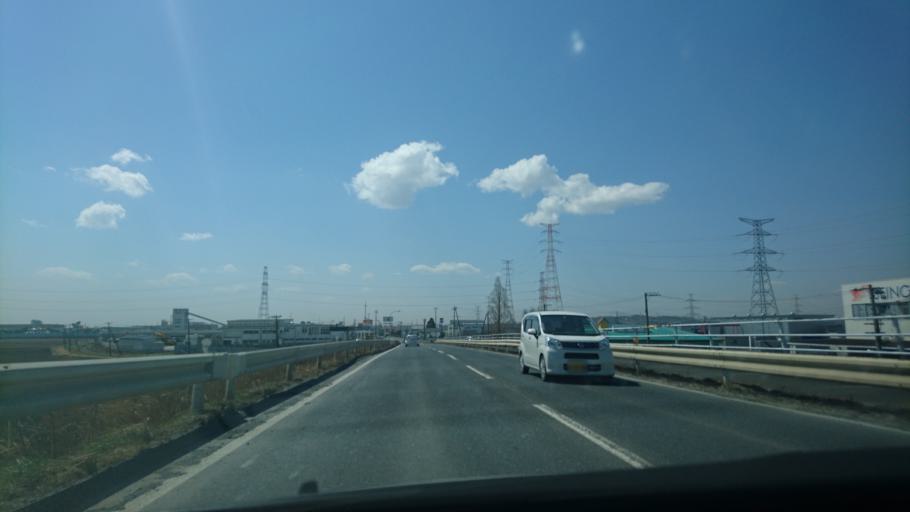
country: JP
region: Miyagi
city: Ishinomaki
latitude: 38.4803
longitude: 141.2868
